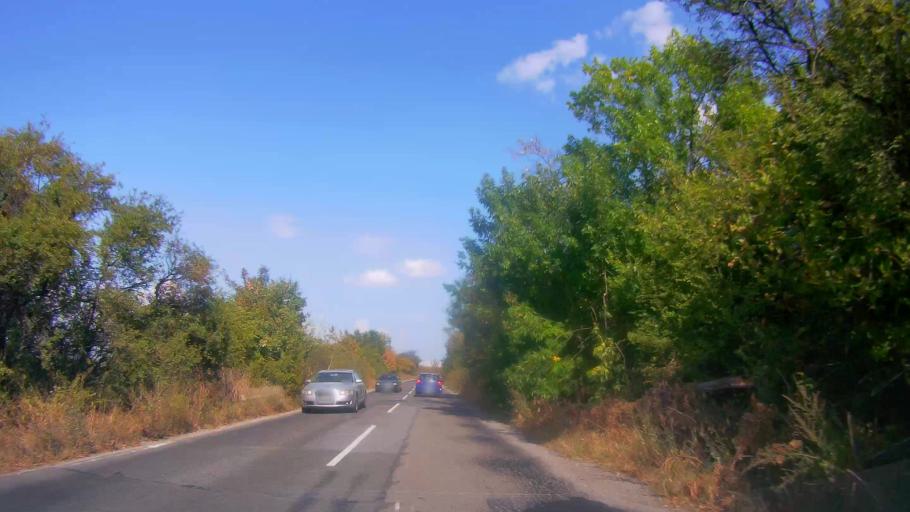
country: BG
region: Burgas
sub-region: Obshtina Burgas
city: Burgas
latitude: 42.4757
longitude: 27.4016
